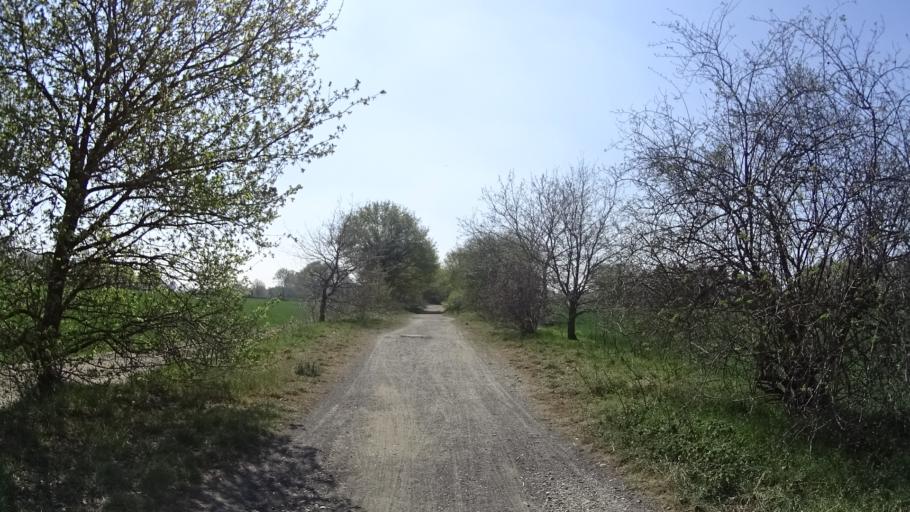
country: DE
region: North Rhine-Westphalia
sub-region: Regierungsbezirk Dusseldorf
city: Moers
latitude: 51.3926
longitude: 6.6297
